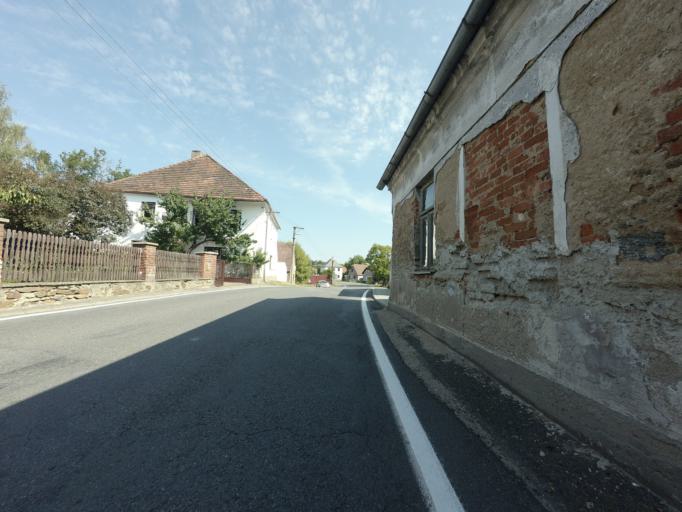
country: CZ
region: Jihocesky
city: Bernartice
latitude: 49.3890
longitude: 14.3578
